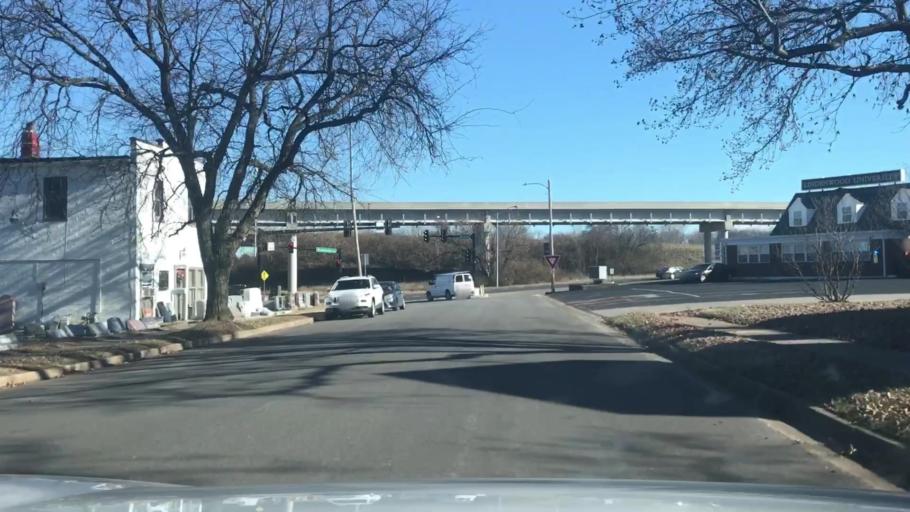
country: US
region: Missouri
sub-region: Saint Charles County
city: Wentzville
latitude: 38.8119
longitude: -90.8434
